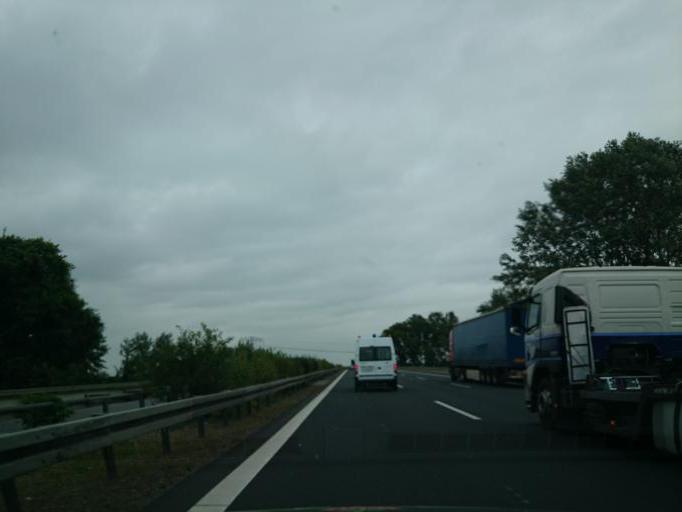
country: DE
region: Brandenburg
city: Grossbeeren
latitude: 52.3061
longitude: 13.3330
